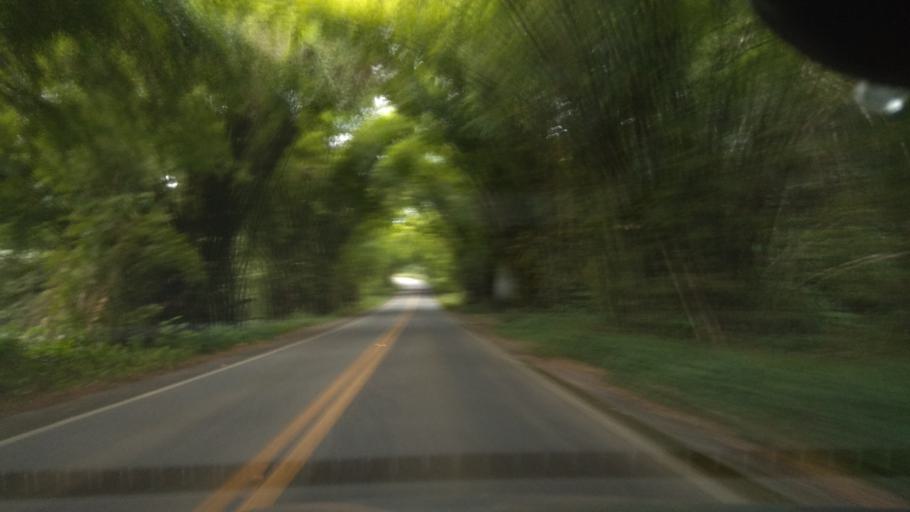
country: BR
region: Bahia
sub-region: Ibirapitanga
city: Ibirapitanga
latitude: -14.2355
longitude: -39.3850
